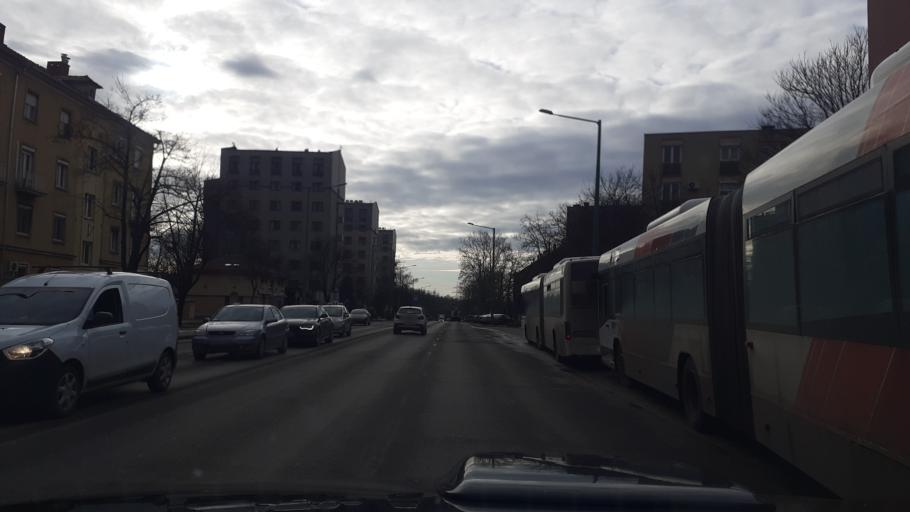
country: HU
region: Fejer
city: dunaujvaros
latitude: 46.9620
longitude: 18.9330
